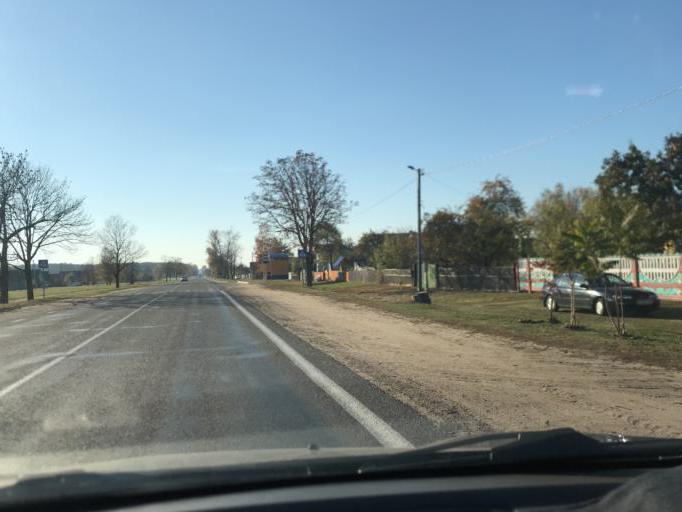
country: BY
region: Minsk
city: Staryya Darohi
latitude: 53.0404
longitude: 28.3177
